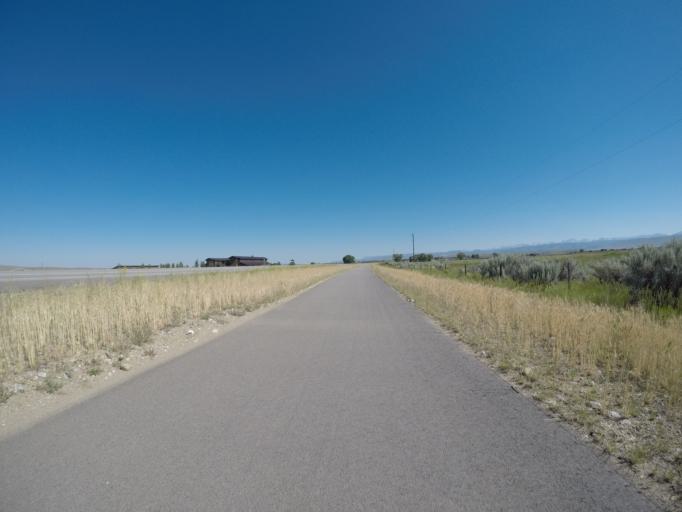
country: US
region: Wyoming
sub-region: Sublette County
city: Pinedale
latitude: 42.8296
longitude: -109.8457
